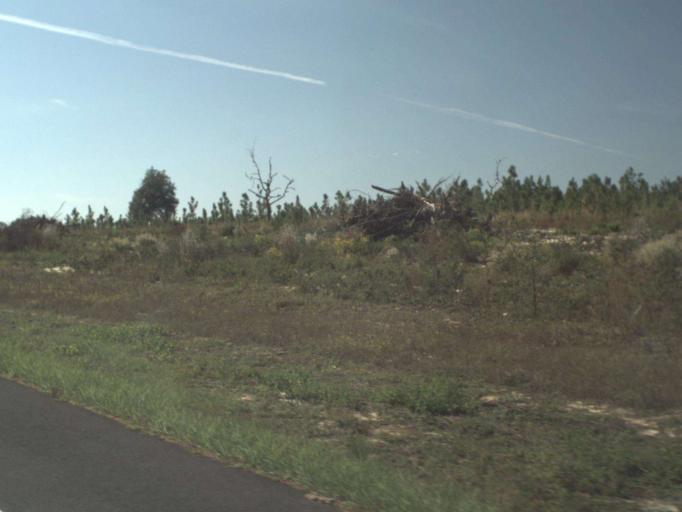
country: US
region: Florida
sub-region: Gadsden County
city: Gretna
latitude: 30.4683
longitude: -84.7351
